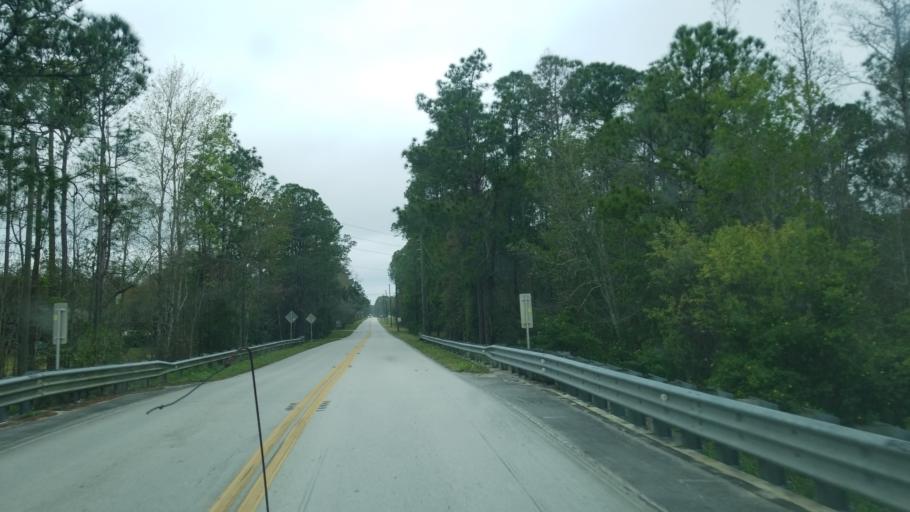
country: US
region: Florida
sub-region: Lake County
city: Four Corners
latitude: 28.2553
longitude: -81.6750
